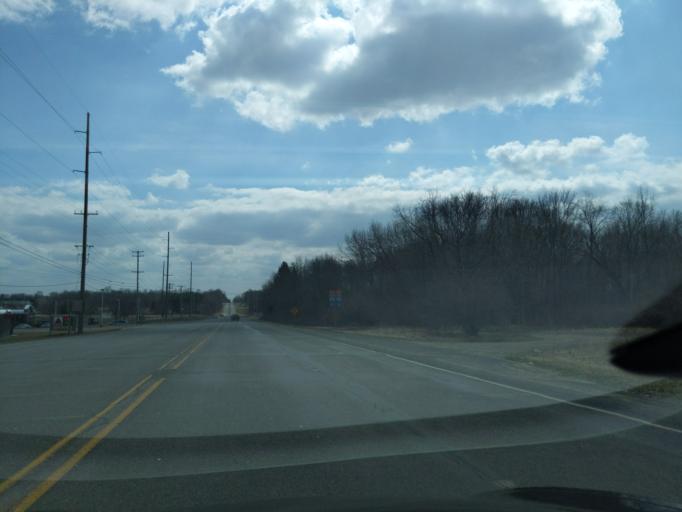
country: US
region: Michigan
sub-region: Calhoun County
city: Marshall
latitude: 42.2926
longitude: -84.9645
